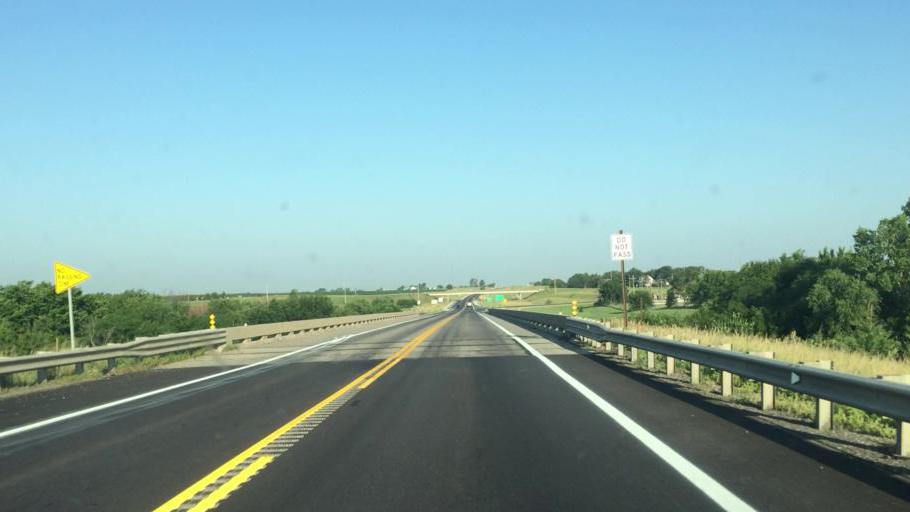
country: US
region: Kansas
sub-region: Brown County
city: Hiawatha
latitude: 39.8408
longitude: -95.5378
